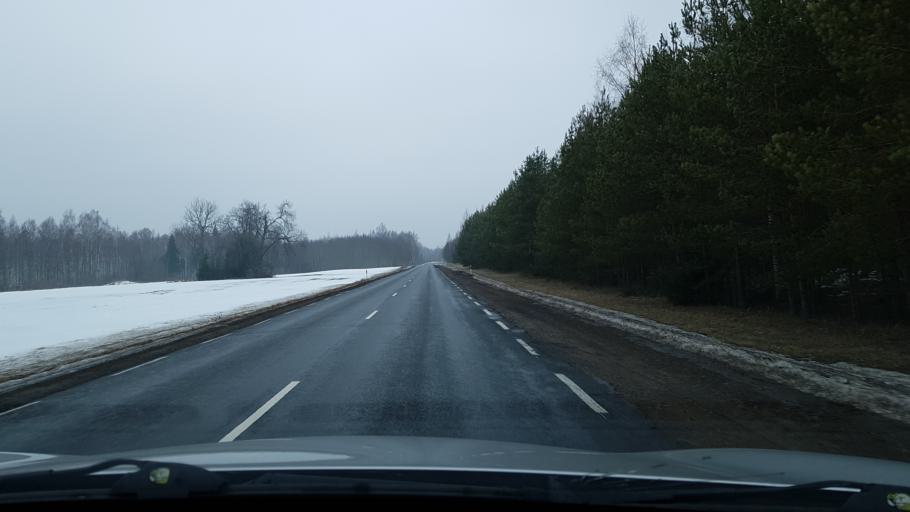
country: EE
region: Valgamaa
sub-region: Torva linn
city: Torva
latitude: 58.1132
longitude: 26.0007
